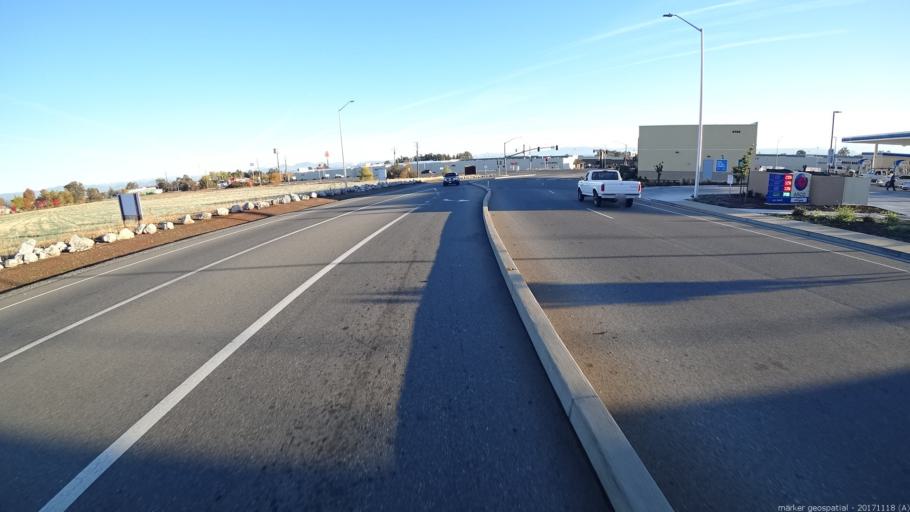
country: US
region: California
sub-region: Shasta County
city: Anderson
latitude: 40.4339
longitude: -122.2896
